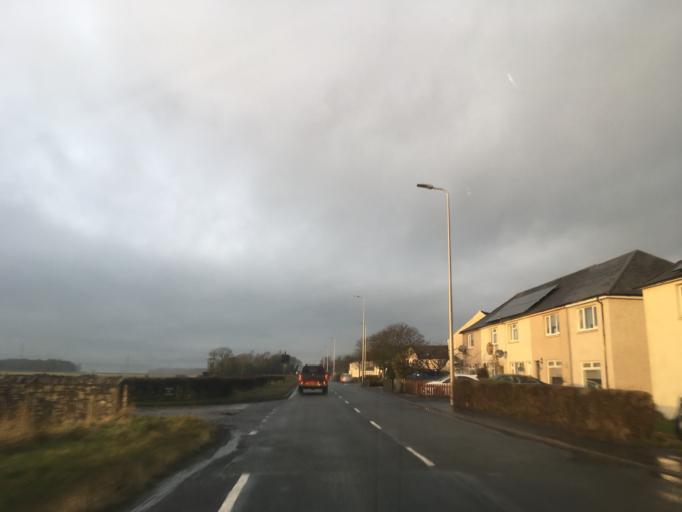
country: GB
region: Scotland
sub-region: Stirling
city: Cowie
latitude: 56.0991
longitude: -3.8410
